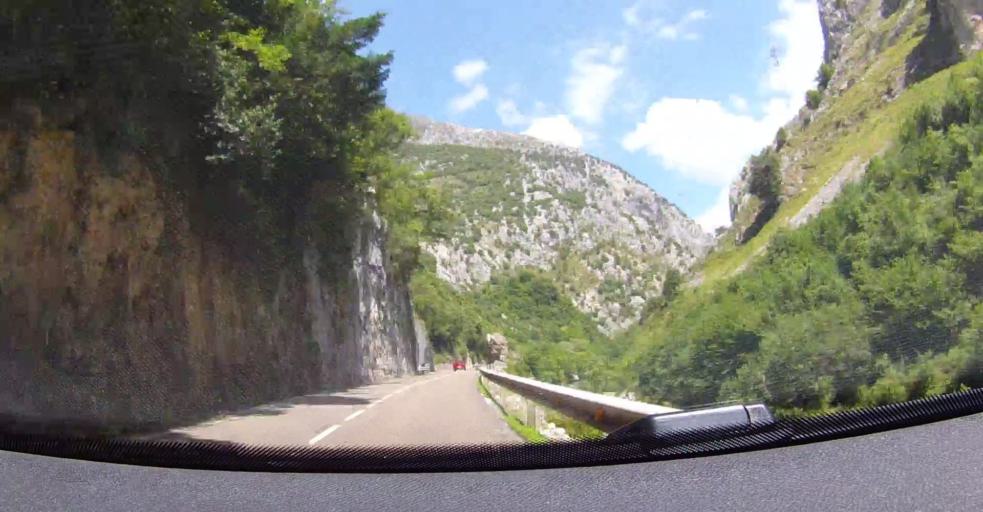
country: ES
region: Cantabria
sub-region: Provincia de Cantabria
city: Tresviso
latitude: 43.2846
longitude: -4.6263
